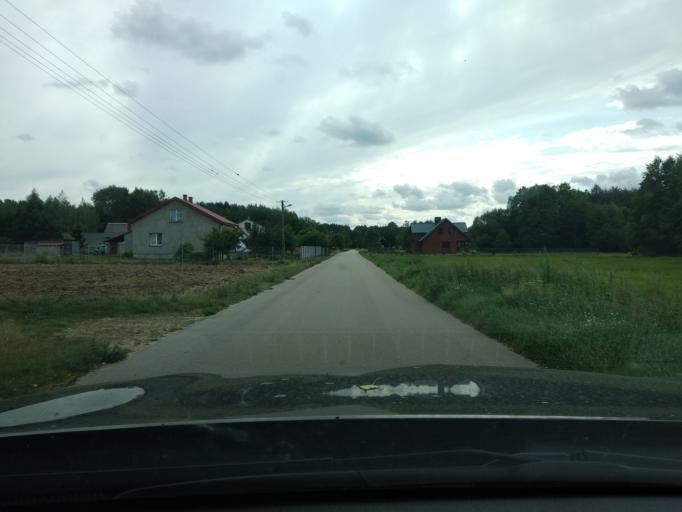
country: PL
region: Masovian Voivodeship
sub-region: Powiat pultuski
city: Pultusk
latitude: 52.7310
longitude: 21.1635
